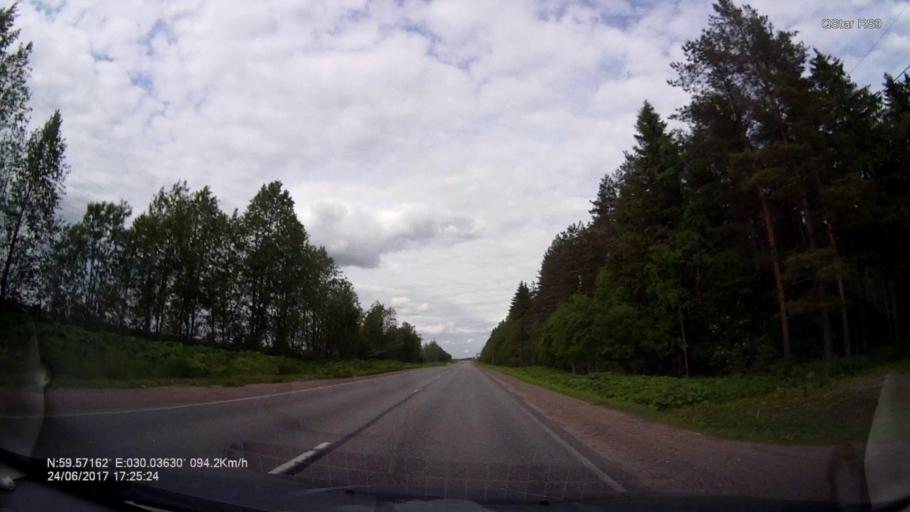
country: RU
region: Leningrad
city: Mariyenburg
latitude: 59.5718
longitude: 30.0367
